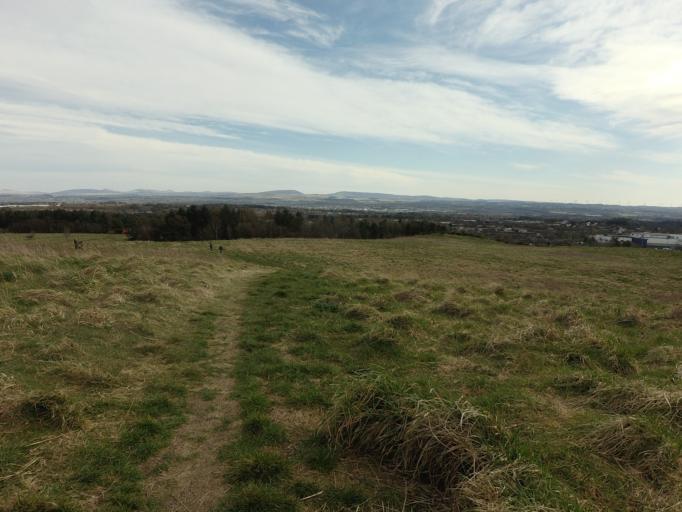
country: GB
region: Scotland
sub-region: West Lothian
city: Livingston
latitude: 55.9104
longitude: -3.5484
